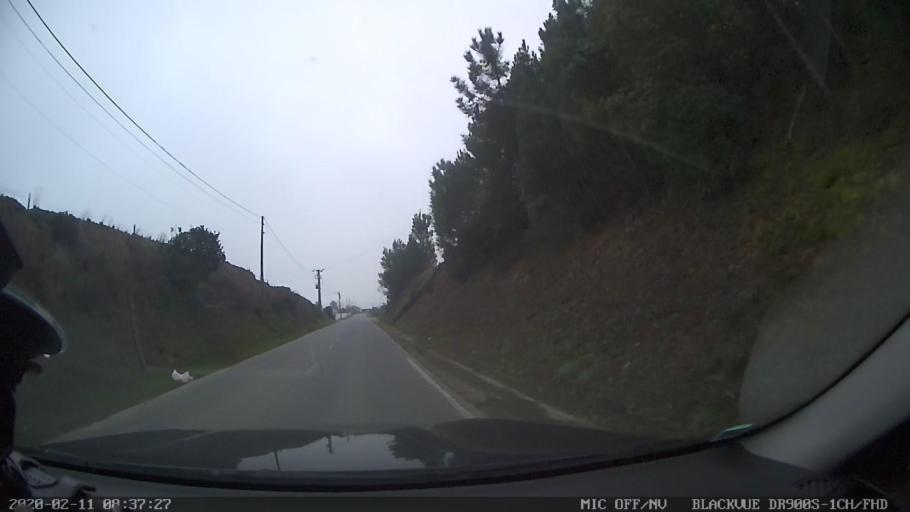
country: PT
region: Vila Real
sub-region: Sabrosa
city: Sabrosa
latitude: 41.2574
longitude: -7.5896
